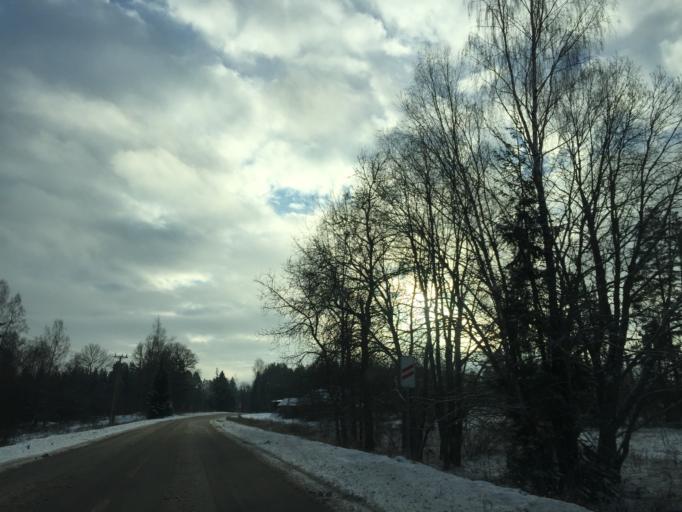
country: LV
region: Amatas Novads
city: Drabesi
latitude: 57.2280
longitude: 25.2791
